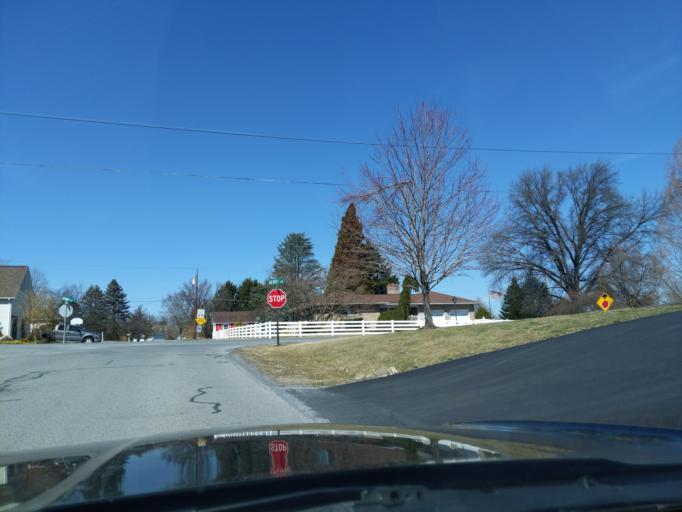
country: US
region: Pennsylvania
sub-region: Blair County
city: Duncansville
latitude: 40.4144
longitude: -78.4204
